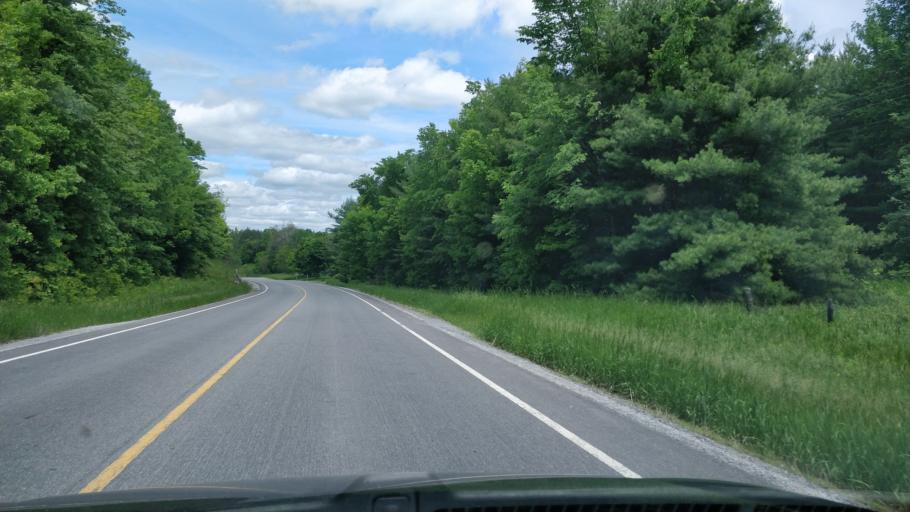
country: CA
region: Ontario
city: Perth
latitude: 44.7767
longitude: -76.4510
